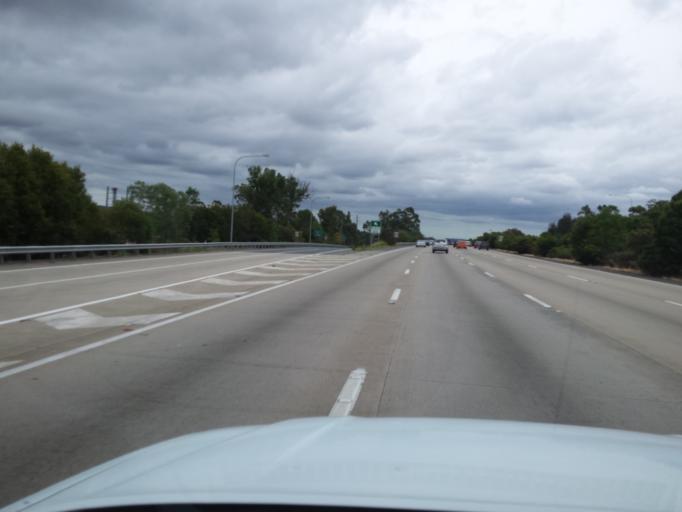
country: AU
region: Queensland
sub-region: Gold Coast
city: Upper Coomera
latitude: -27.9128
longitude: 153.3189
